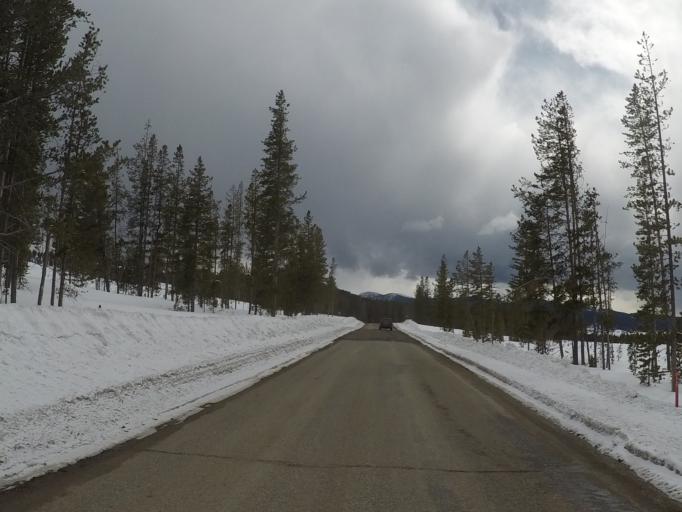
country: US
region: Montana
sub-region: Granite County
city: Philipsburg
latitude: 46.2046
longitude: -113.2518
